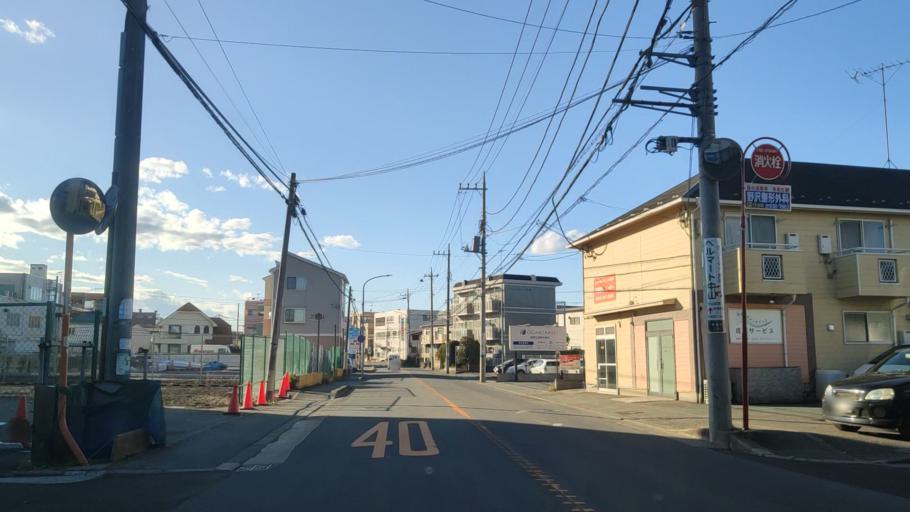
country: JP
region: Tokyo
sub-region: Machida-shi
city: Machida
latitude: 35.5185
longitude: 139.5477
